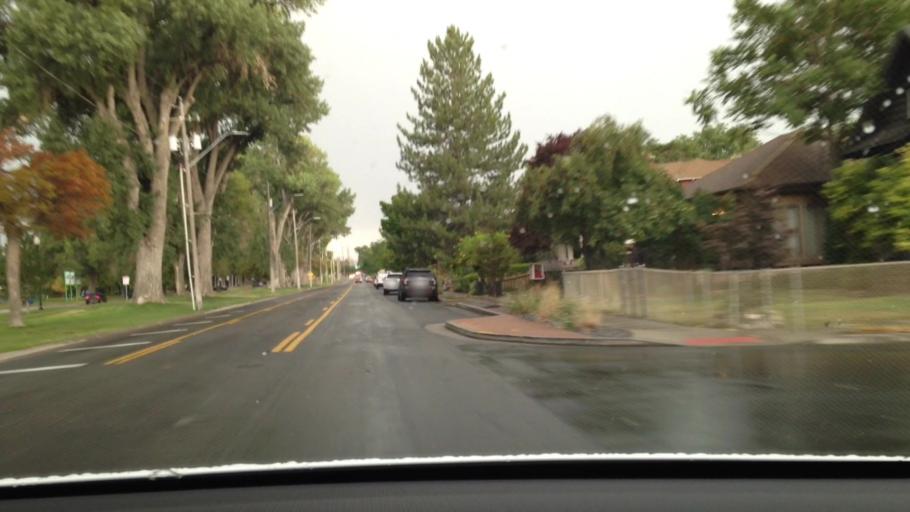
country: US
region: Utah
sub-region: Salt Lake County
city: Salt Lake City
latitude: 40.7465
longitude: -111.8768
